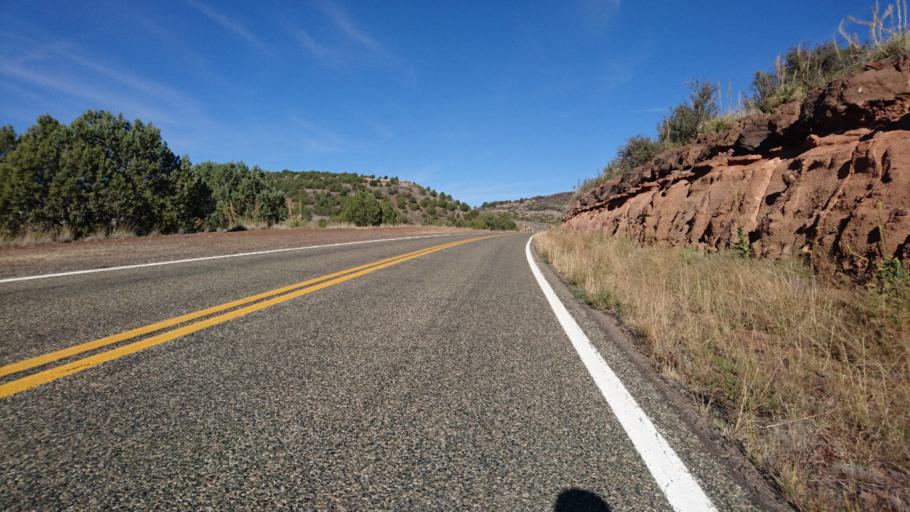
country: US
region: Arizona
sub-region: Yavapai County
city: Paulden
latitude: 35.2743
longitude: -112.6882
